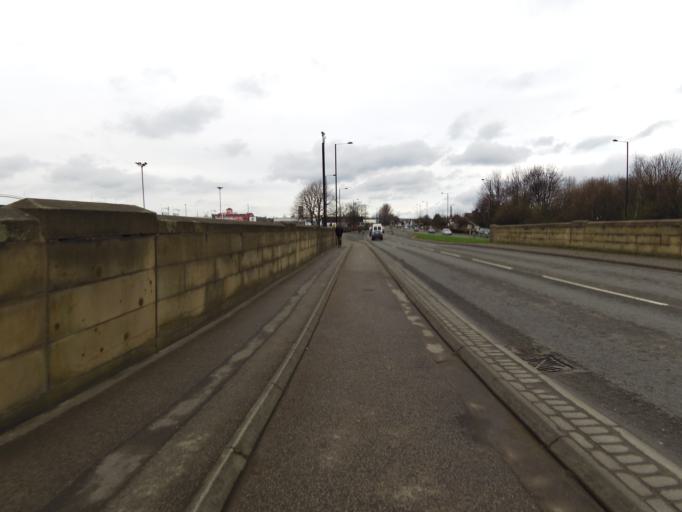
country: GB
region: England
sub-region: Doncaster
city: Bentley
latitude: 53.5318
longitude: -1.1529
